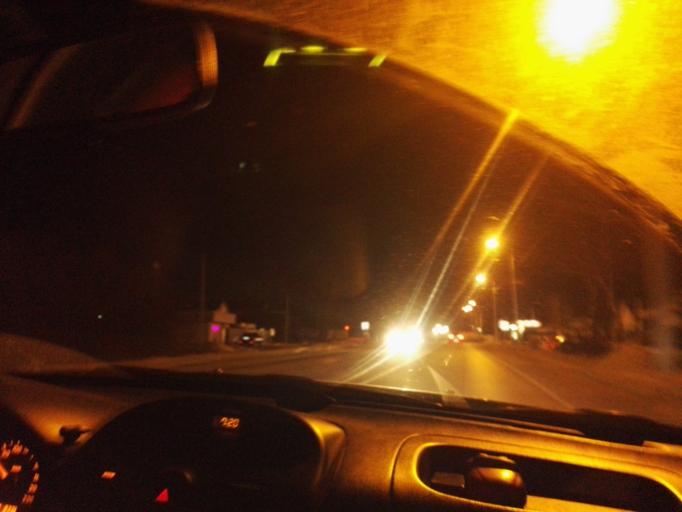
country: RU
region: Tula
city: Skuratovskiy
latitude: 54.1359
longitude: 37.6775
